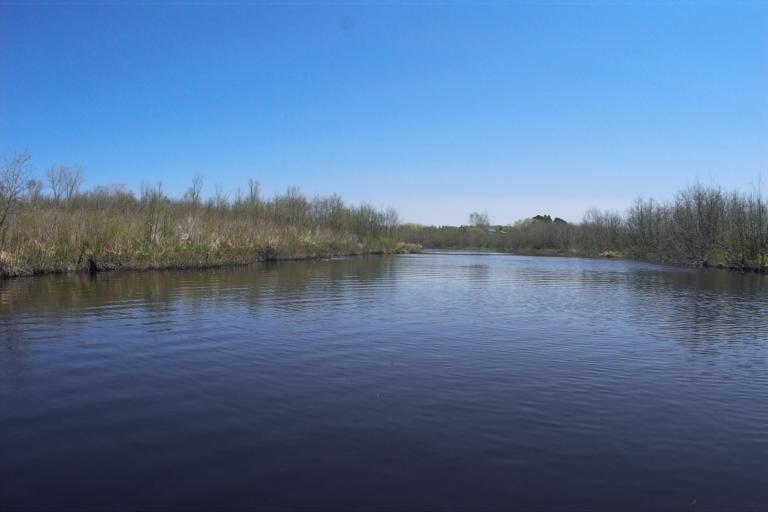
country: CA
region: Ontario
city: Powassan
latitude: 46.1583
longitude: -79.2523
